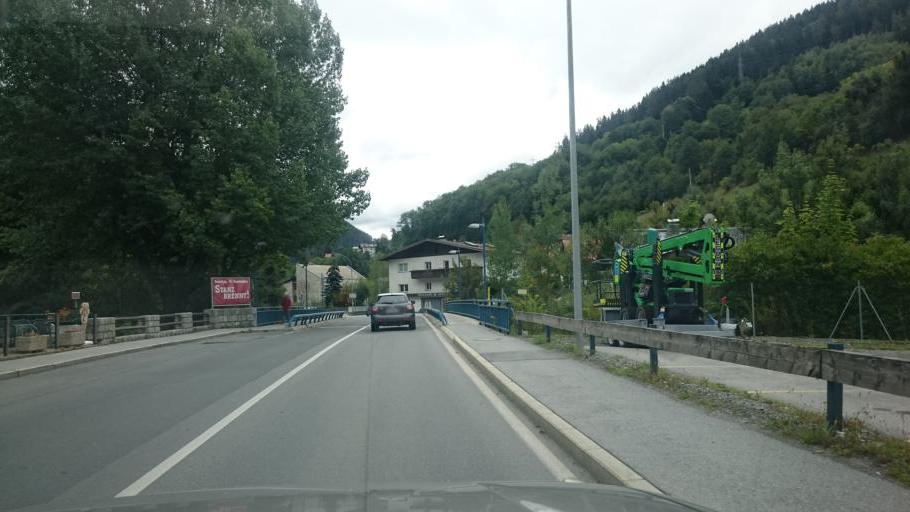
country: AT
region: Tyrol
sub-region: Politischer Bezirk Landeck
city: Stanz bei Landeck
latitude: 47.1409
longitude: 10.5536
